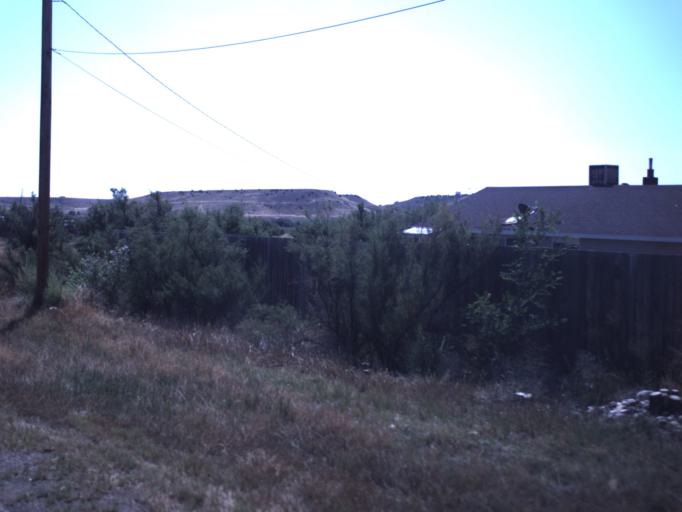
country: US
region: Utah
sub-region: Duchesne County
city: Roosevelt
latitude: 40.2585
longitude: -110.0861
